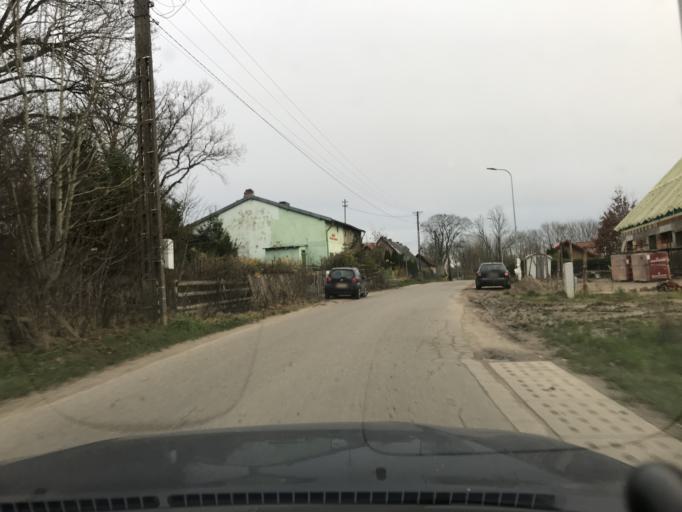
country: PL
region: Pomeranian Voivodeship
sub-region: Powiat slupski
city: Kobylnica
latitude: 54.4462
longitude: 16.8872
